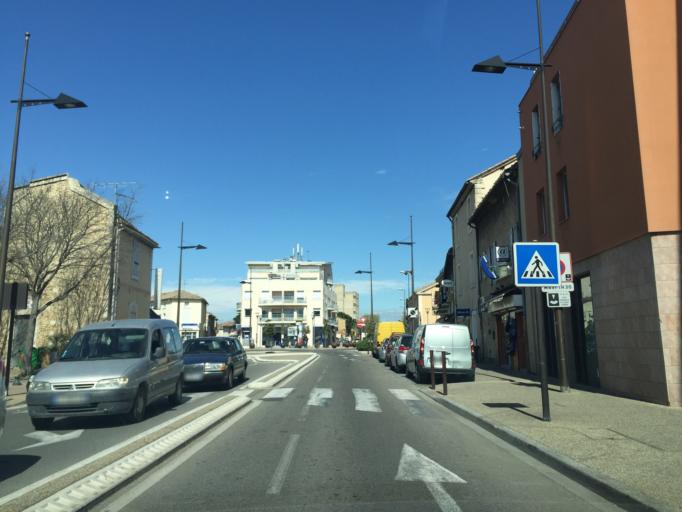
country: FR
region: Provence-Alpes-Cote d'Azur
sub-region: Departement du Vaucluse
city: Le Pontet
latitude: 43.9614
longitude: 4.8580
